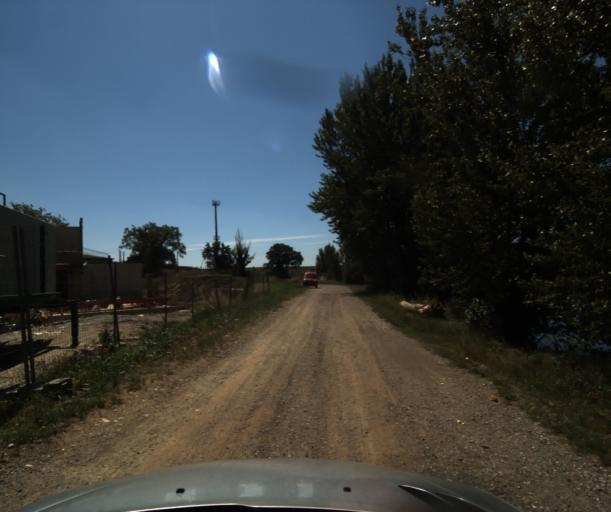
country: FR
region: Midi-Pyrenees
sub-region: Departement de la Haute-Garonne
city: Roquettes
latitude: 43.4926
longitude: 1.3675
